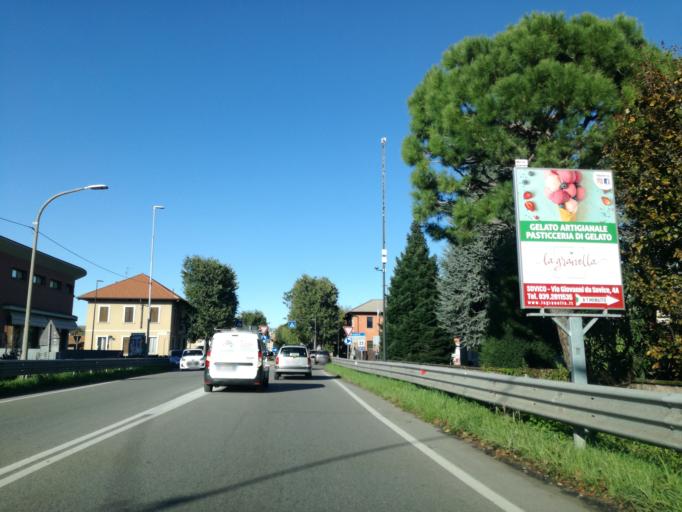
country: IT
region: Lombardy
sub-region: Provincia di Monza e Brianza
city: Sovico
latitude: 45.6453
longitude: 9.2607
